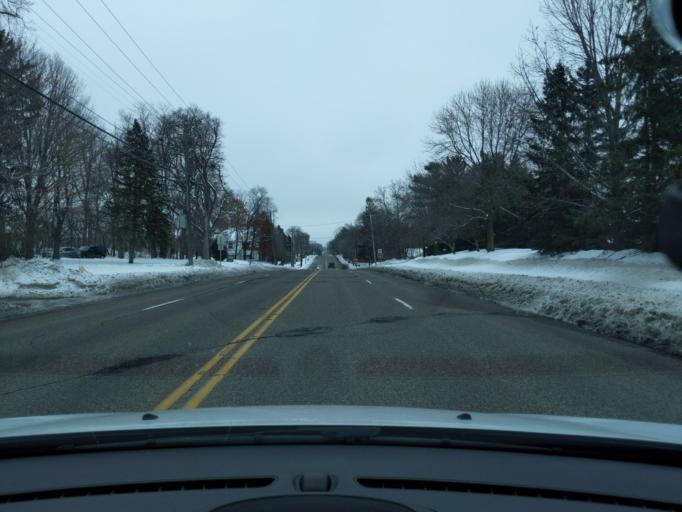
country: US
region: Minnesota
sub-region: Ramsey County
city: Roseville
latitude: 45.0207
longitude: -93.1284
